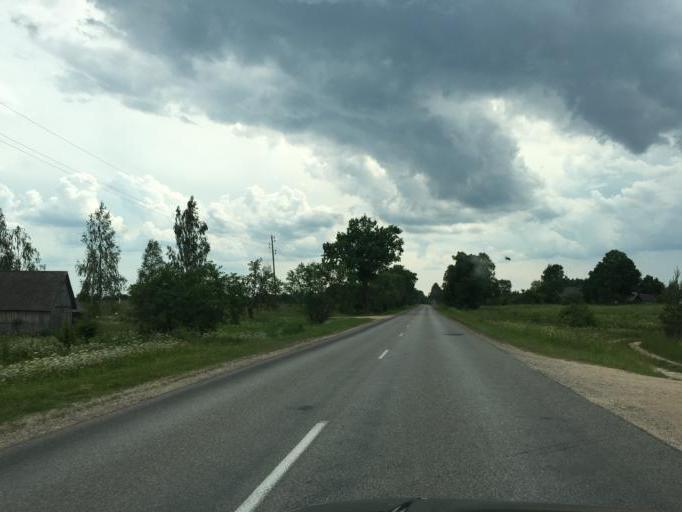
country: LV
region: Rugaju
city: Rugaji
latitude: 56.9149
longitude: 27.0689
